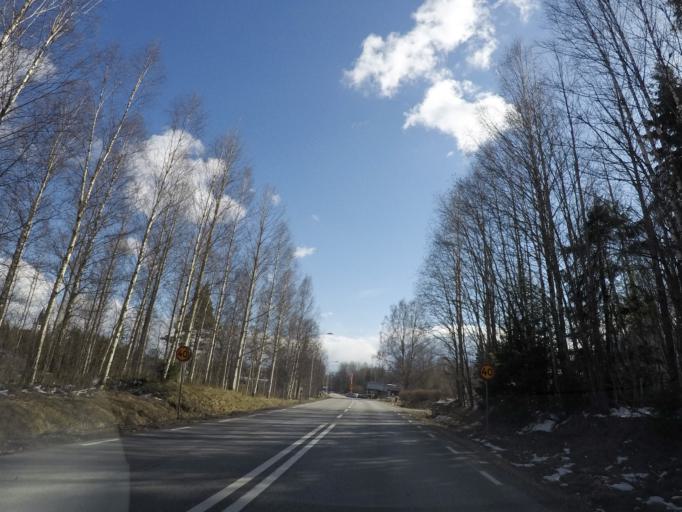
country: SE
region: Vaestmanland
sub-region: Skinnskattebergs Kommun
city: Skinnskatteberg
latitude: 59.8332
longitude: 15.6763
